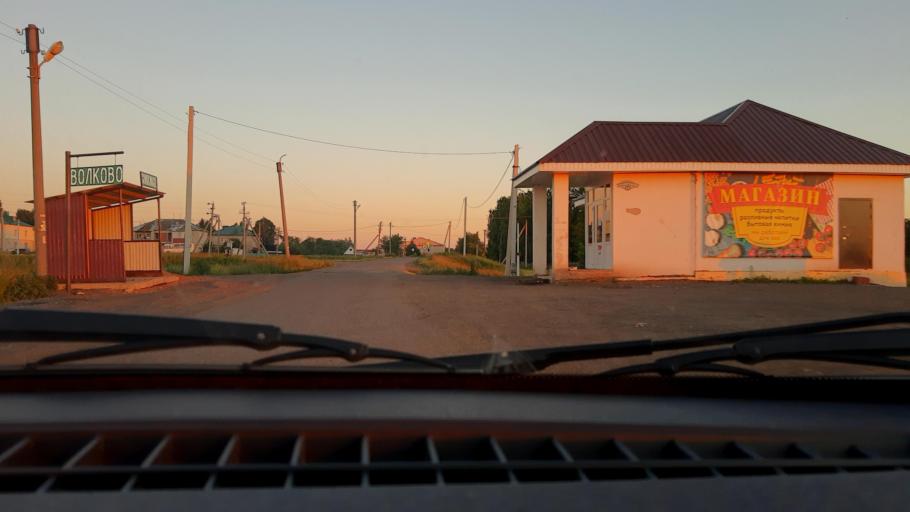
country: RU
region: Bashkortostan
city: Asanovo
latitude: 54.8913
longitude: 55.6245
